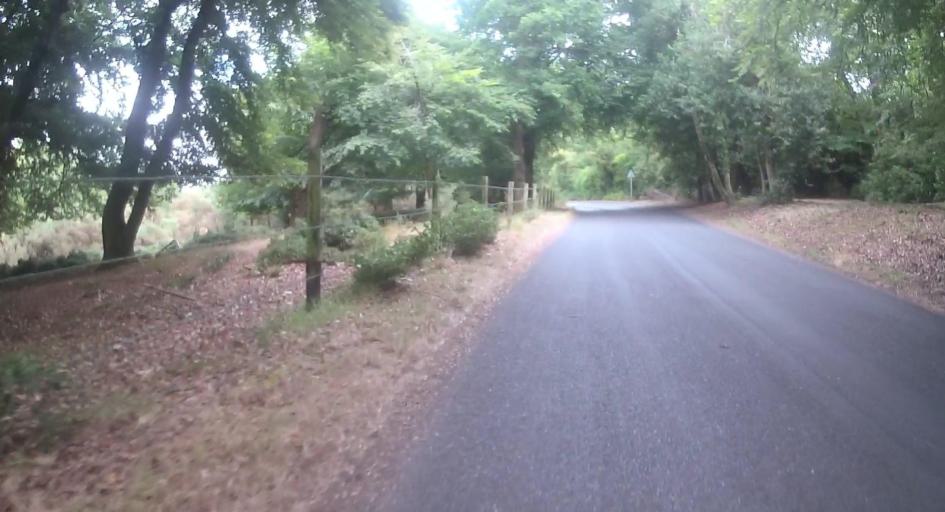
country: GB
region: England
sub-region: Dorset
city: Wareham
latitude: 50.6698
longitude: -2.1335
